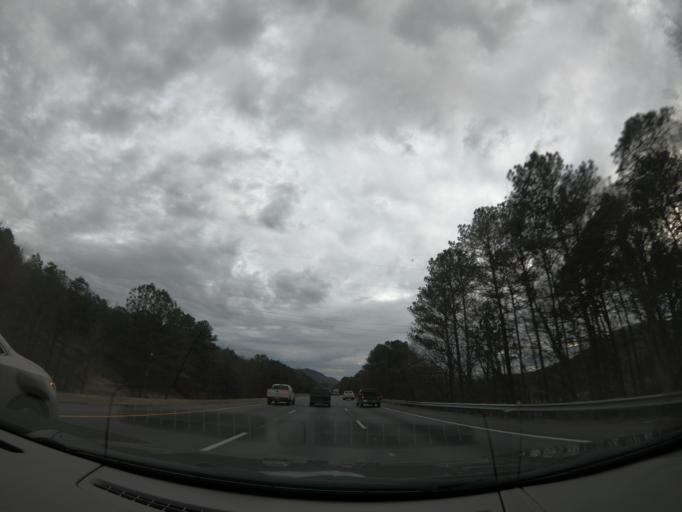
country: US
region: Georgia
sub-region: Whitfield County
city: Dalton
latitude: 34.8235
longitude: -85.0180
